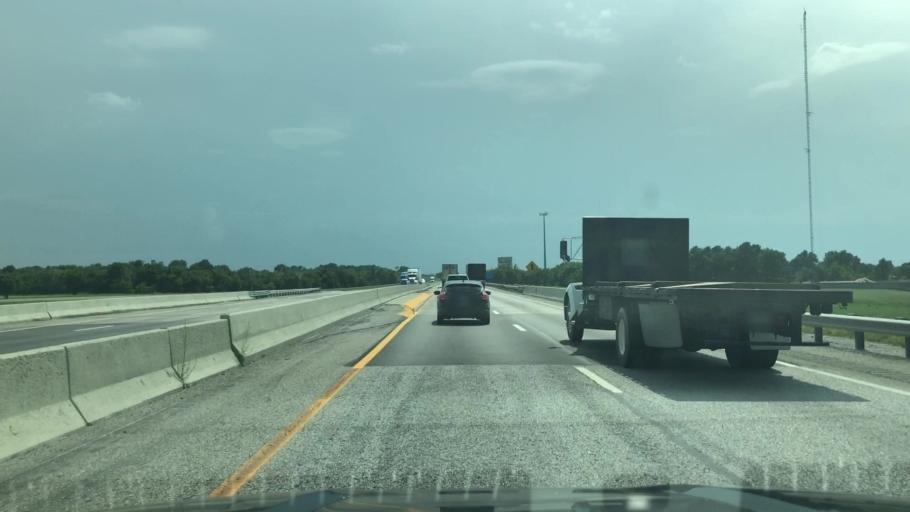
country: US
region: Oklahoma
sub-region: Craig County
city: Vinita
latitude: 36.6330
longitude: -95.1326
